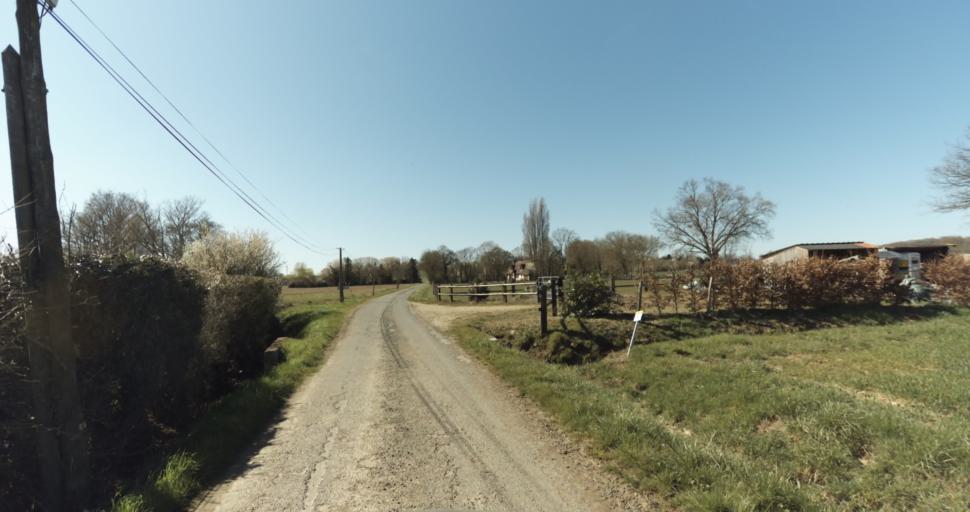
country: FR
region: Lower Normandy
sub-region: Departement du Calvados
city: Saint-Pierre-sur-Dives
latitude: 49.0545
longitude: -0.0015
